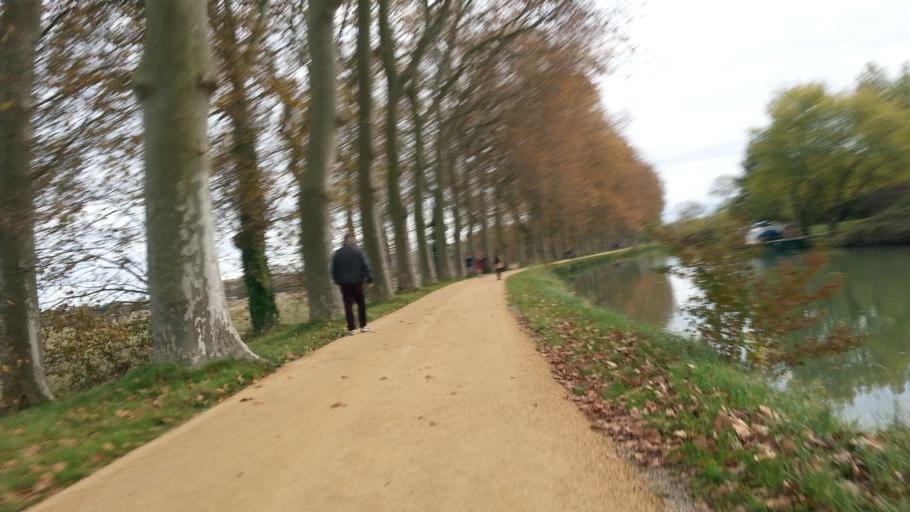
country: FR
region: Midi-Pyrenees
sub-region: Departement de la Haute-Garonne
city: Castanet-Tolosan
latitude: 43.5345
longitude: 1.5050
